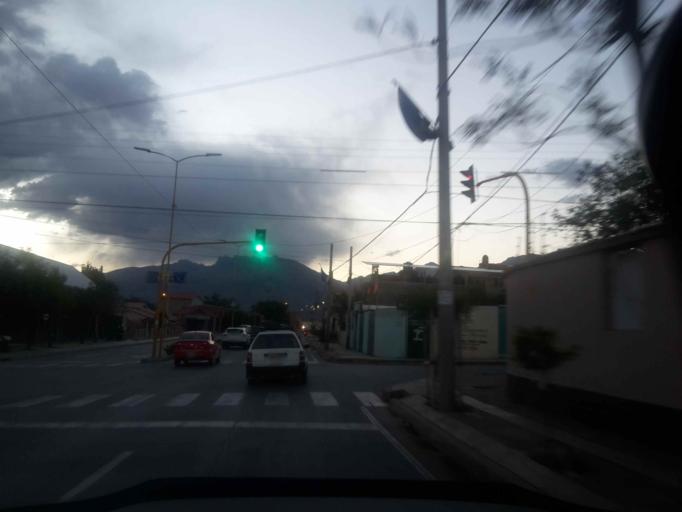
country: BO
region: Cochabamba
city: Cochabamba
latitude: -17.3466
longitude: -66.1949
